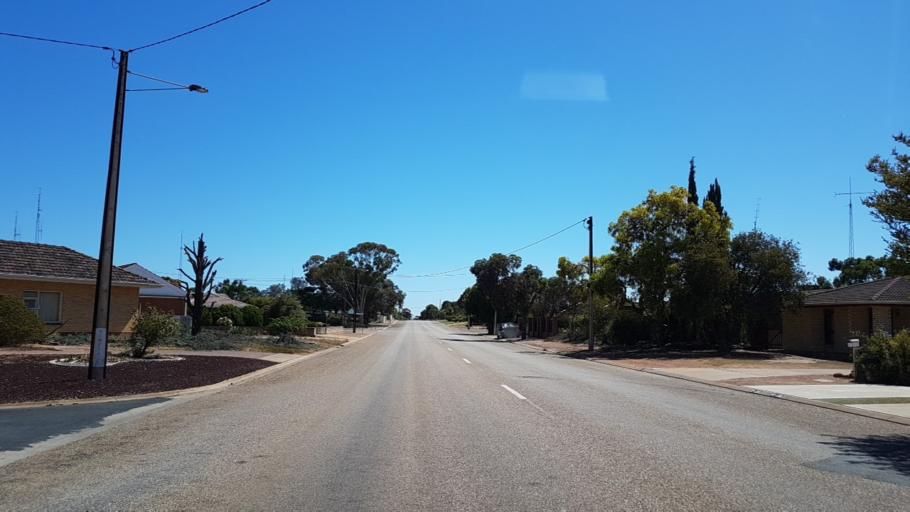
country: AU
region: South Australia
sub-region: Copper Coast
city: Kadina
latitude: -33.9637
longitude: 137.7236
